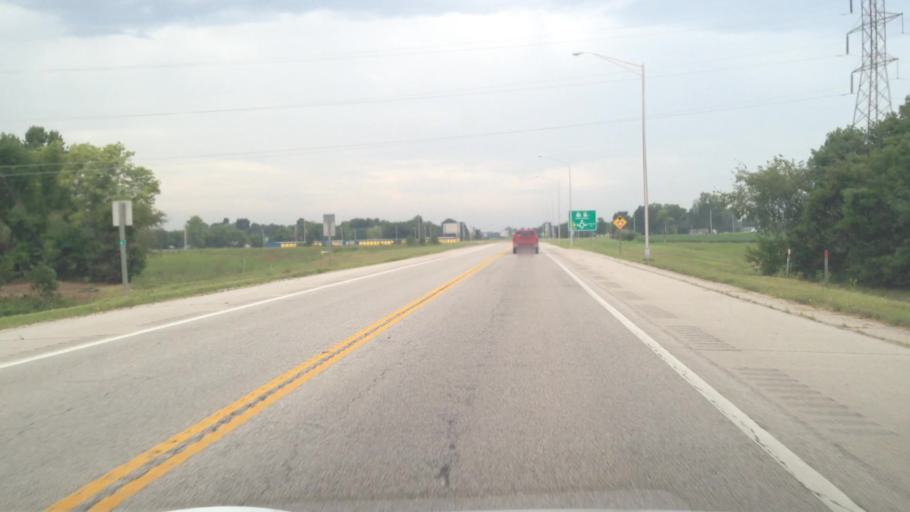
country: US
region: Kansas
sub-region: Cherokee County
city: Baxter Springs
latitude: 37.0783
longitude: -94.7130
